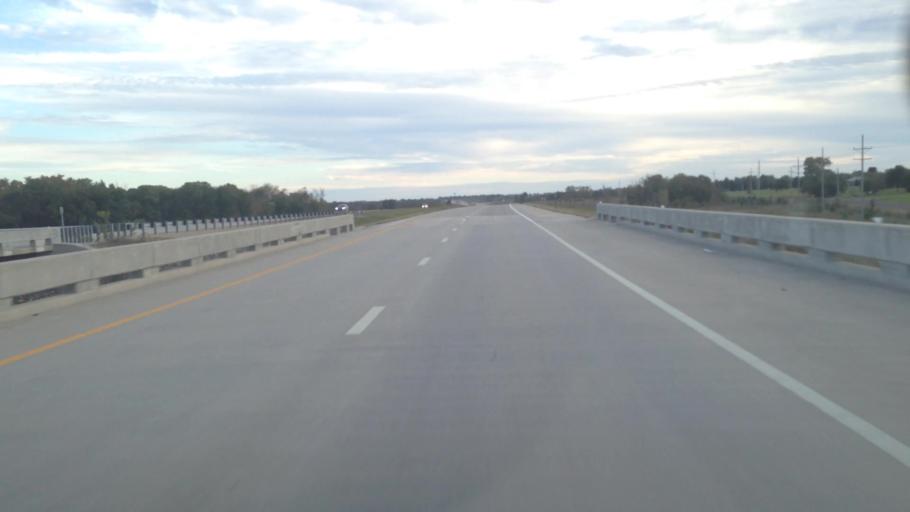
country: US
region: Kansas
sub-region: Douglas County
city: Baldwin City
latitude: 38.7388
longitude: -95.2678
